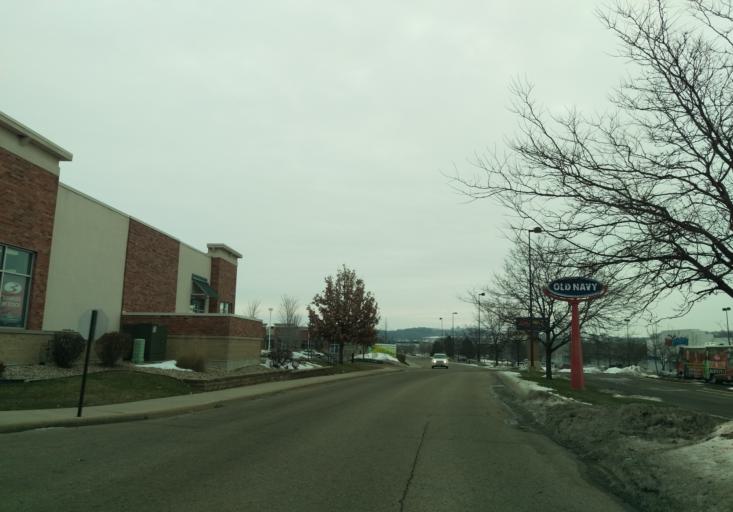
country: US
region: Wisconsin
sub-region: Dane County
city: Monona
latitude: 43.1302
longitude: -89.2970
